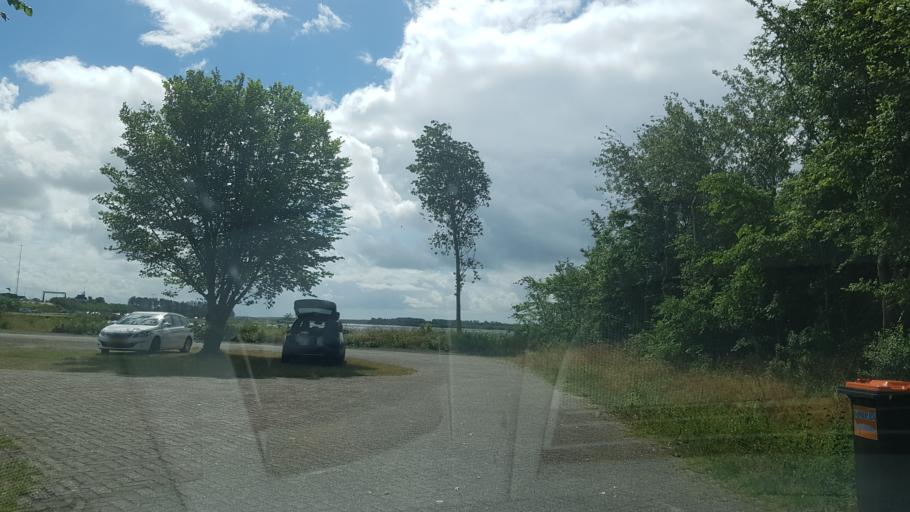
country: NL
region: Friesland
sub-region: Gemeente Dongeradeel
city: Anjum
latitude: 53.4111
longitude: 6.1878
